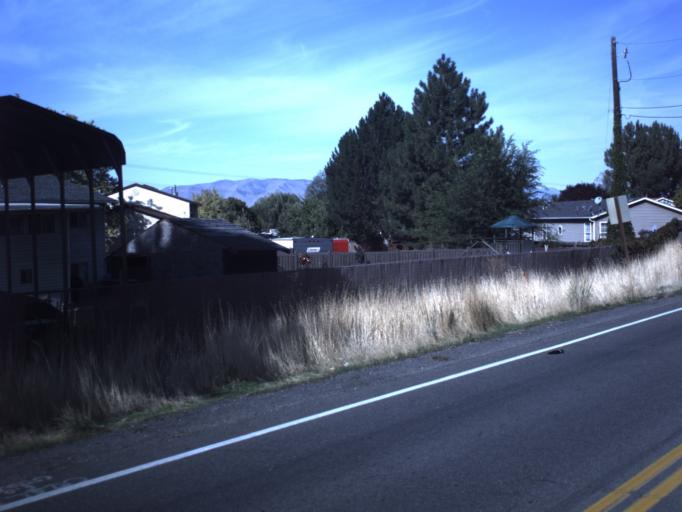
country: US
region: Utah
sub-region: Utah County
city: Provo
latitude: 40.2458
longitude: -111.6984
